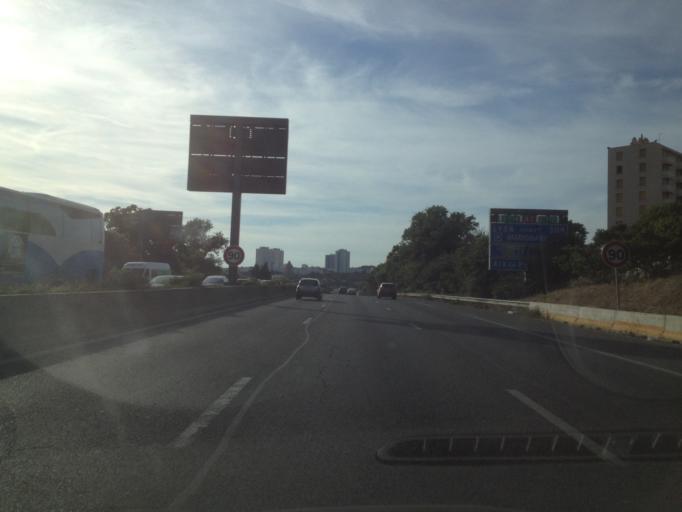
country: FR
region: Provence-Alpes-Cote d'Azur
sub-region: Departement des Bouches-du-Rhone
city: Marseille 14
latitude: 43.3467
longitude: 5.3726
